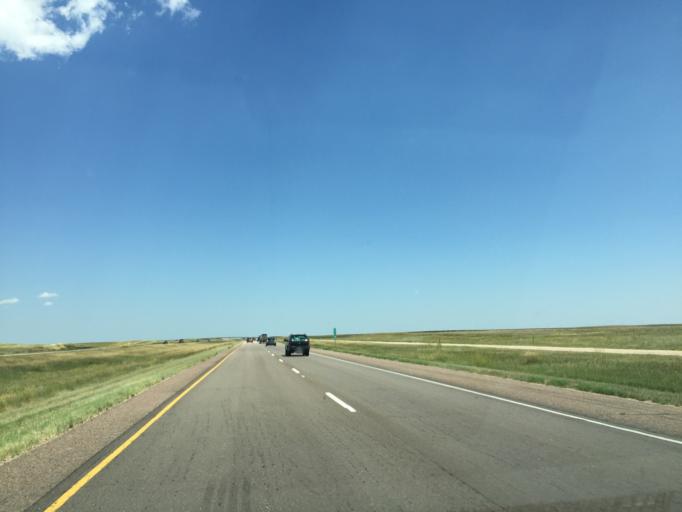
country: US
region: Colorado
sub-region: Lincoln County
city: Hugo
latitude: 39.2800
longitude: -103.3710
